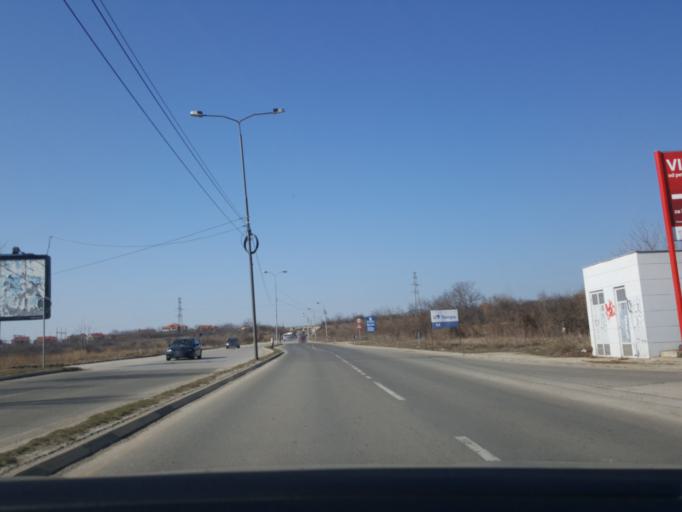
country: RS
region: Central Serbia
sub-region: Nisavski Okrug
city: Nis
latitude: 43.3386
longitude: 21.8880
